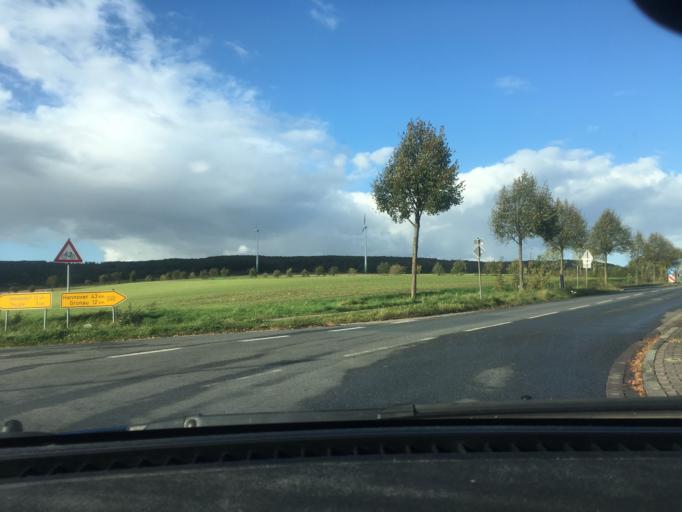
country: DE
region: Lower Saxony
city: Weenzen
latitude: 52.0225
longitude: 9.6721
